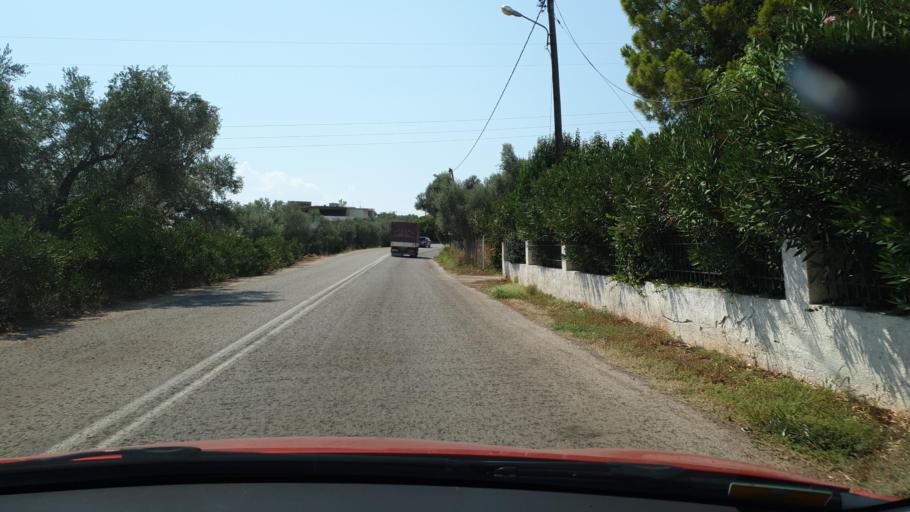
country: GR
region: Central Greece
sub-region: Nomos Evvoias
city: Psachna
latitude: 38.5814
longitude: 23.6175
